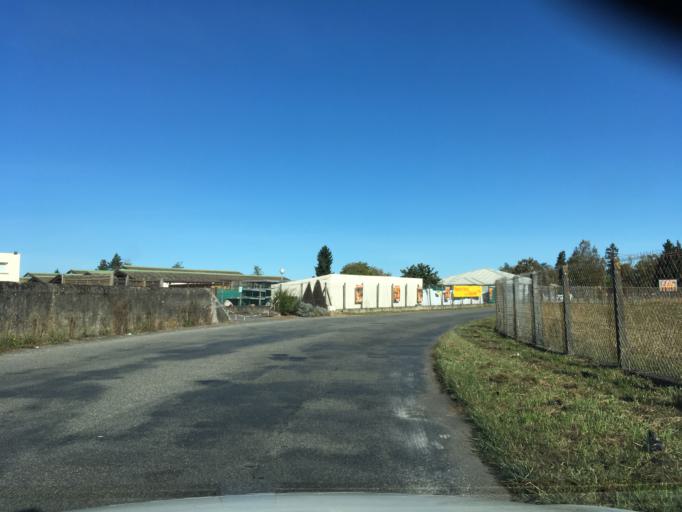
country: FR
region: Aquitaine
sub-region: Departement des Pyrenees-Atlantiques
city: Idron
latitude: 43.3072
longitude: -0.3277
